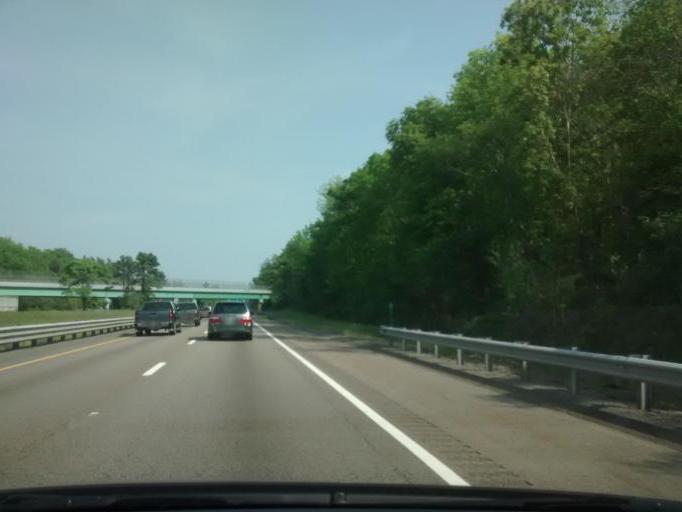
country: US
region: Massachusetts
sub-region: Bristol County
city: Raynham Center
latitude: 41.9199
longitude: -70.9916
